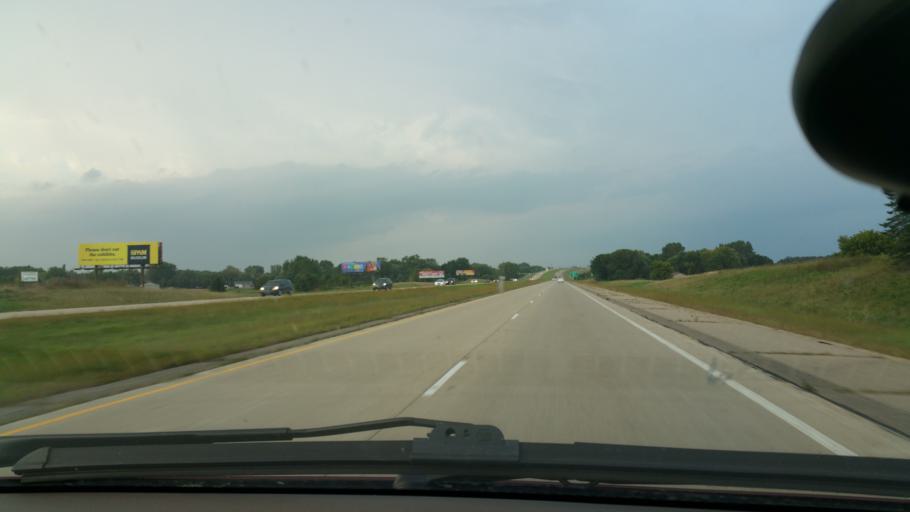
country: US
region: Minnesota
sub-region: Freeborn County
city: Albert Lea
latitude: 43.5981
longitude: -93.3522
